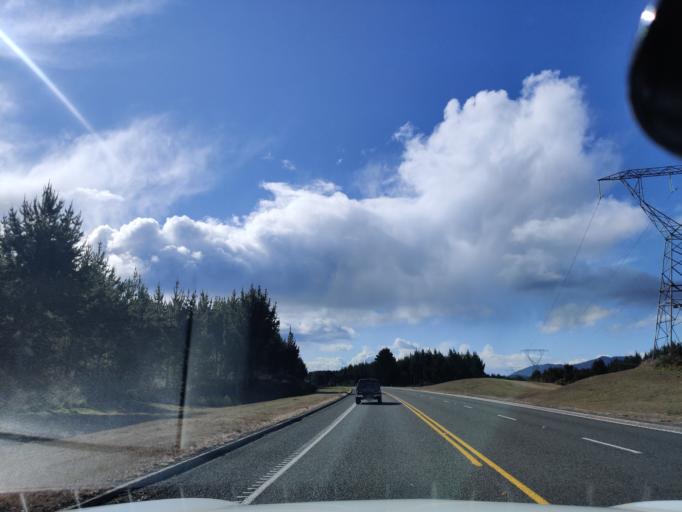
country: NZ
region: Waikato
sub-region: Taupo District
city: Taupo
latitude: -38.8098
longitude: 176.0789
